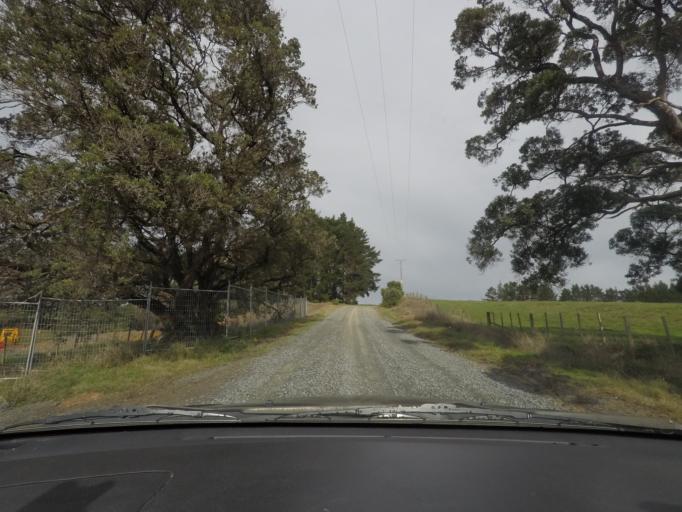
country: NZ
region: Auckland
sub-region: Auckland
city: Warkworth
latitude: -36.4524
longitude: 174.7506
